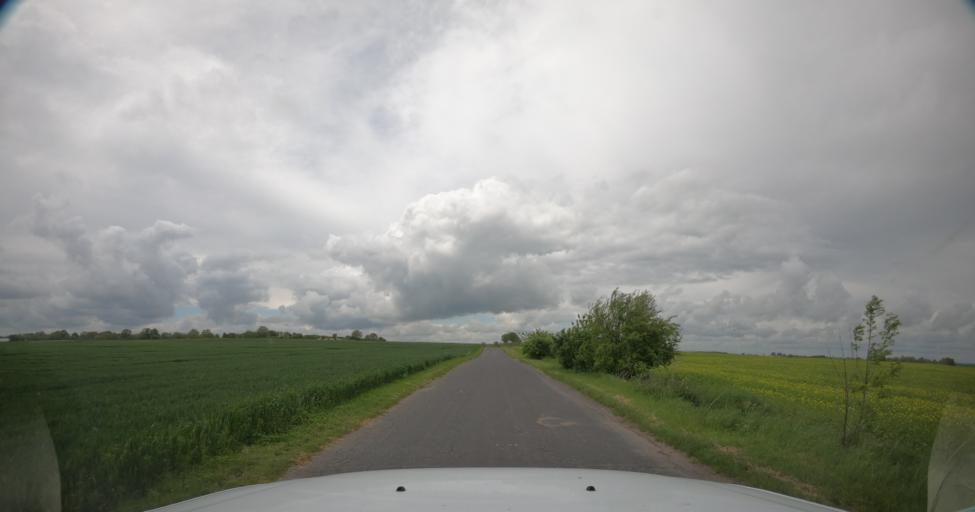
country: PL
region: West Pomeranian Voivodeship
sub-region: Powiat pyrzycki
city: Kozielice
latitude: 53.0788
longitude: 14.8621
